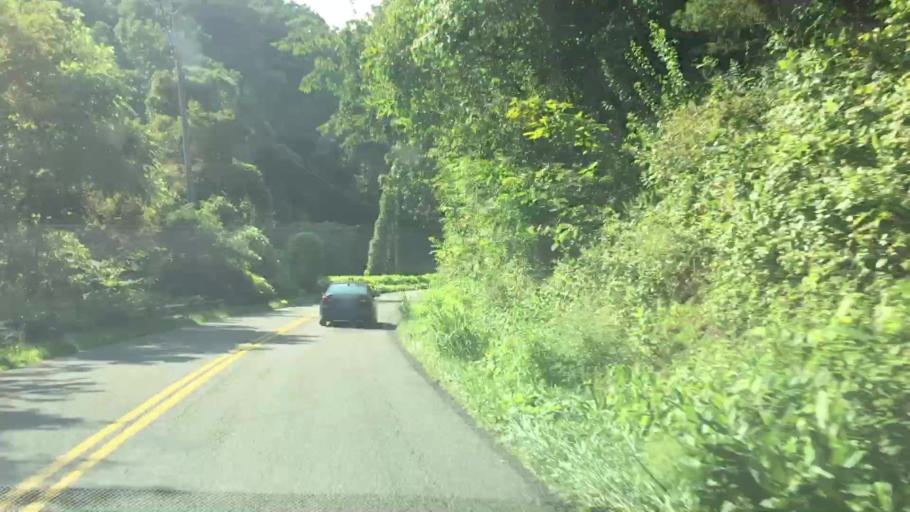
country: US
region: Tennessee
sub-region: Sullivan County
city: Fairmount
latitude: 36.6025
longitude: -82.0691
